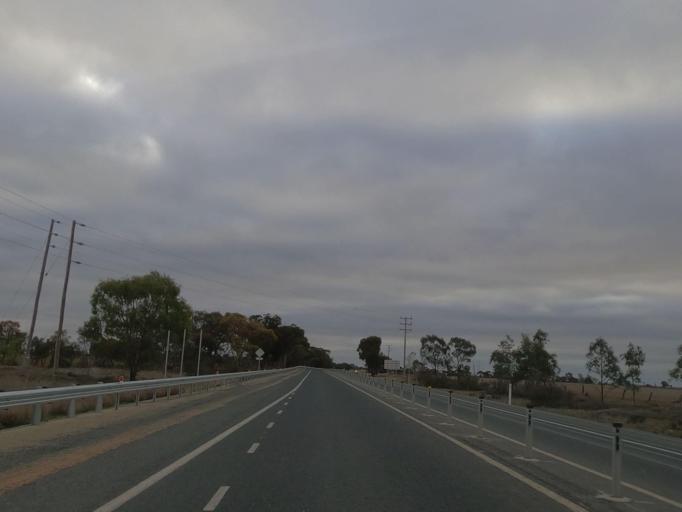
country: AU
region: Victoria
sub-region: Swan Hill
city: Swan Hill
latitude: -35.5492
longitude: 143.7660
